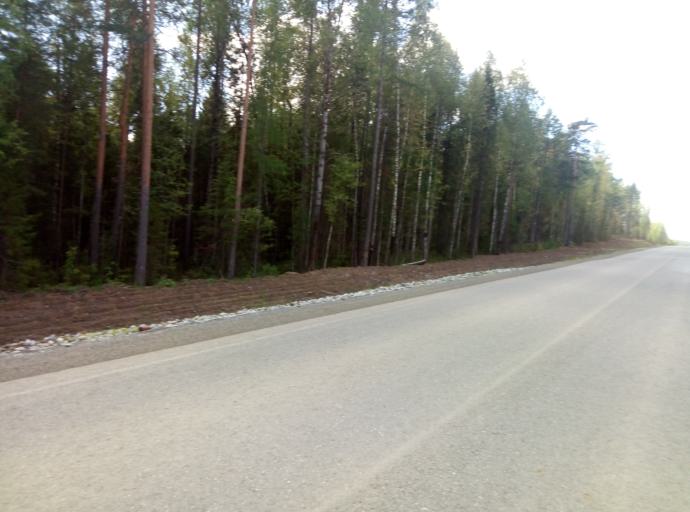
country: RU
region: Sverdlovsk
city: Karpinsk
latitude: 59.6776
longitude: 59.8141
